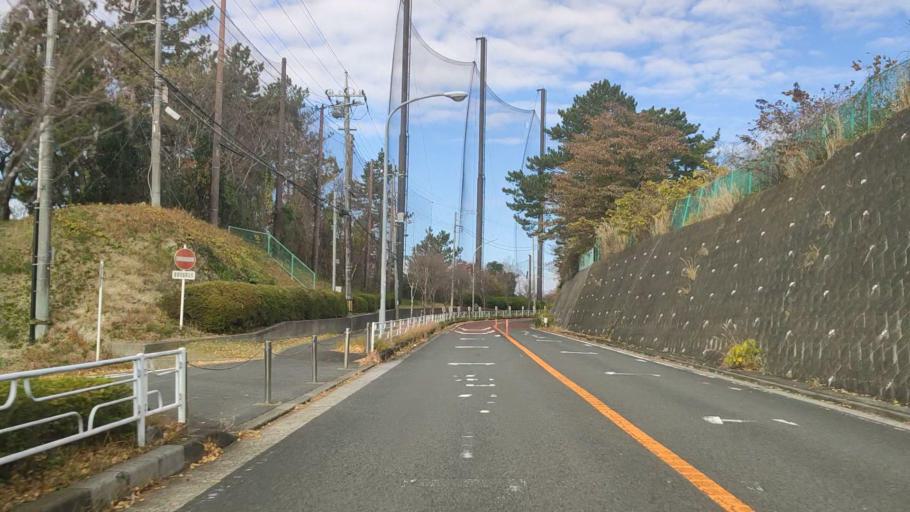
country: JP
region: Kanagawa
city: Minami-rinkan
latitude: 35.4446
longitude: 139.5383
